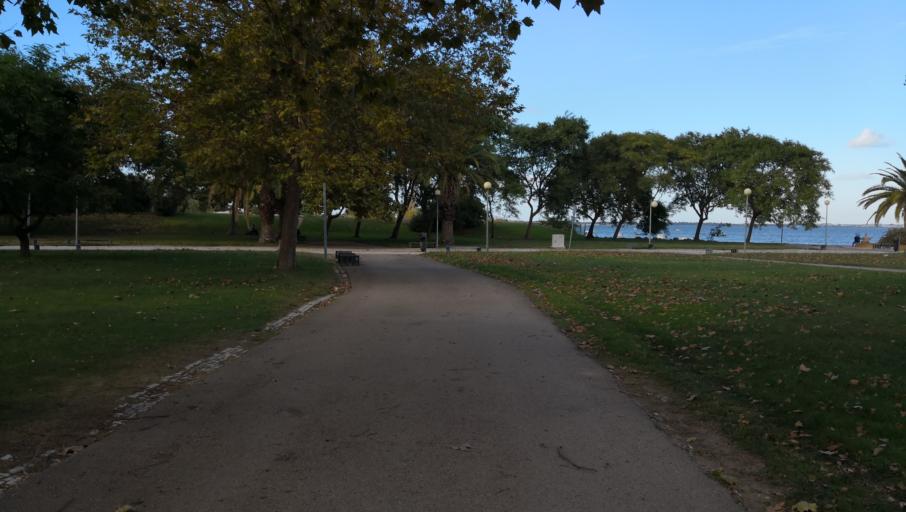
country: PT
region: Setubal
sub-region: Moita
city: Alhos Vedros
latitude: 38.6658
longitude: -9.0440
